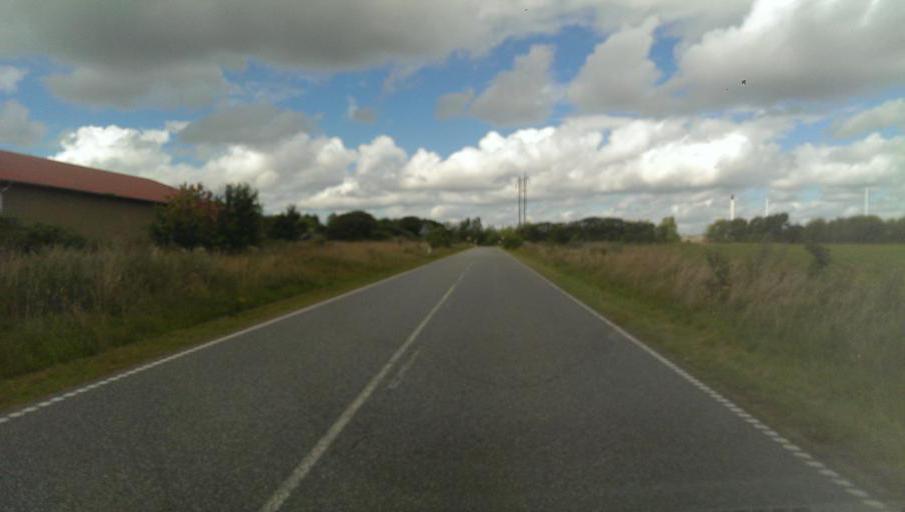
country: DK
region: South Denmark
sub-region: Esbjerg Kommune
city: Tjaereborg
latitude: 55.4639
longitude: 8.5202
